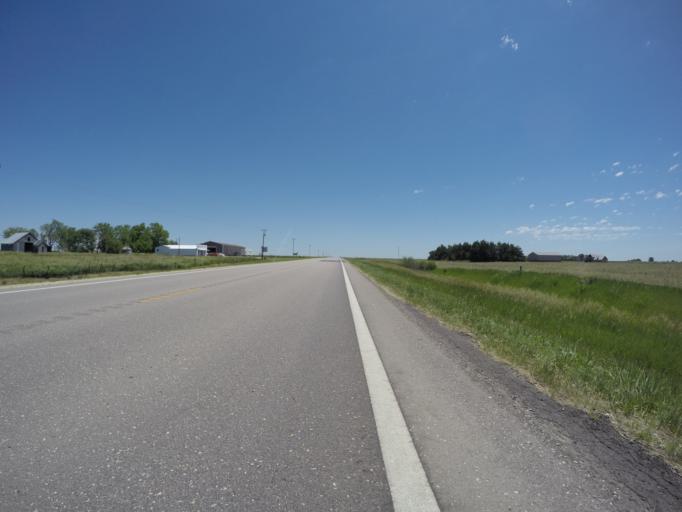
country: US
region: Kansas
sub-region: Republic County
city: Belleville
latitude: 39.8127
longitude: -97.6869
